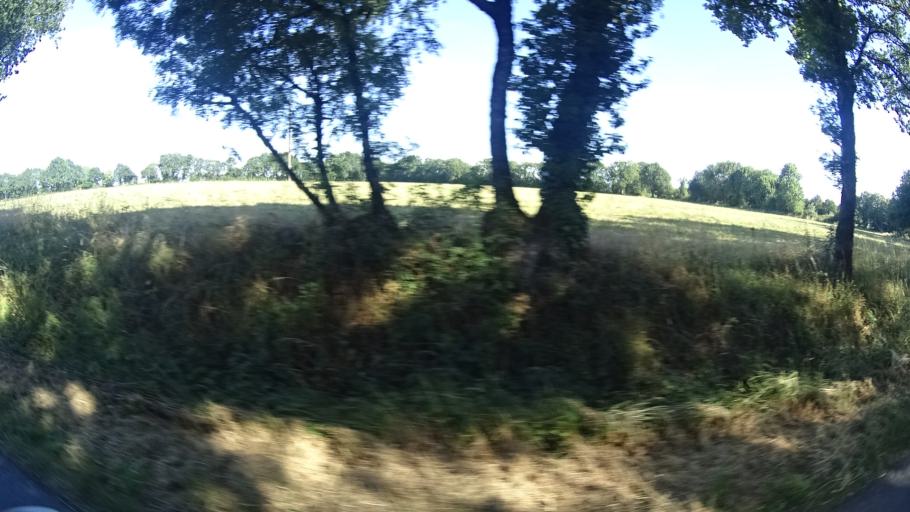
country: FR
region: Brittany
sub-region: Departement d'Ille-et-Vilaine
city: Langon
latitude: 47.7399
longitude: -1.8380
